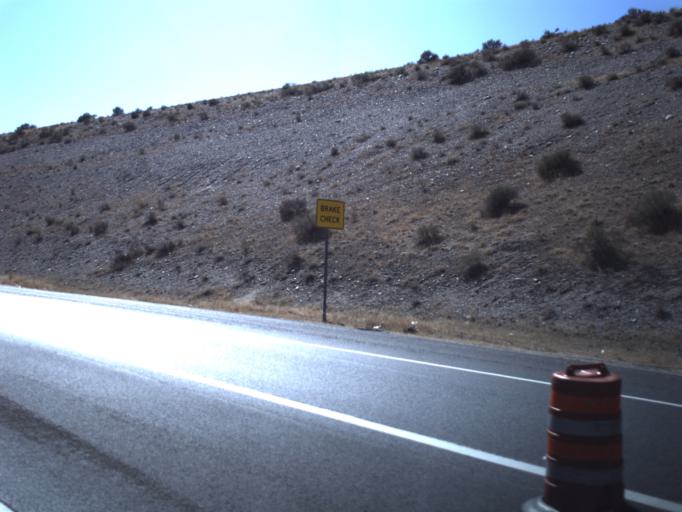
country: US
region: Utah
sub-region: Box Elder County
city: Brigham City
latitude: 41.4977
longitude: -111.9949
